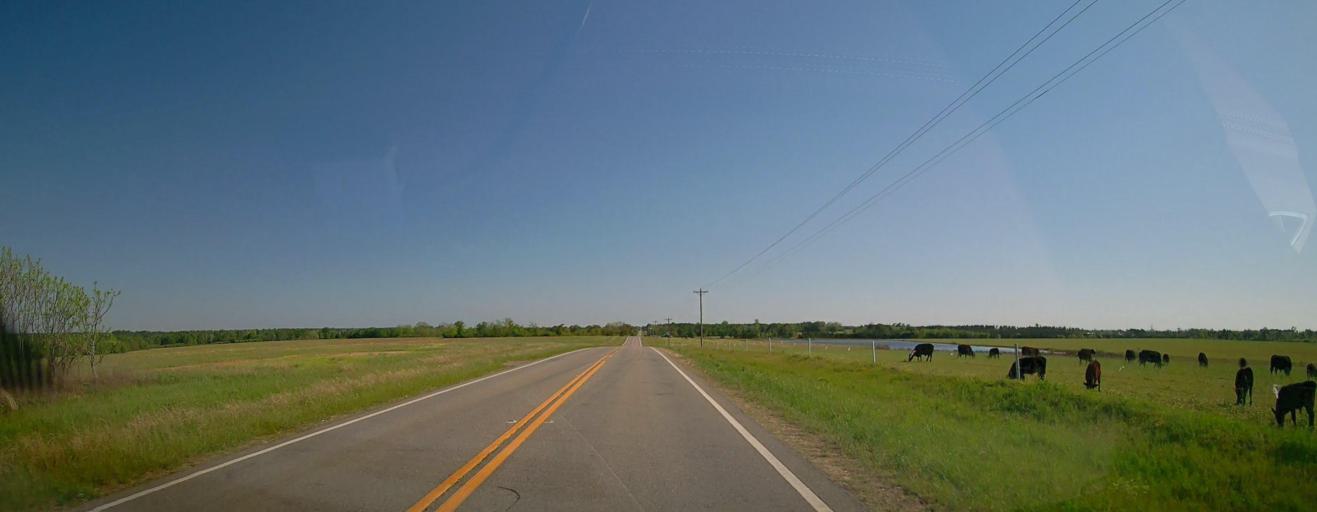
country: US
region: Georgia
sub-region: Wilcox County
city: Rochelle
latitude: 31.8839
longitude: -83.4889
